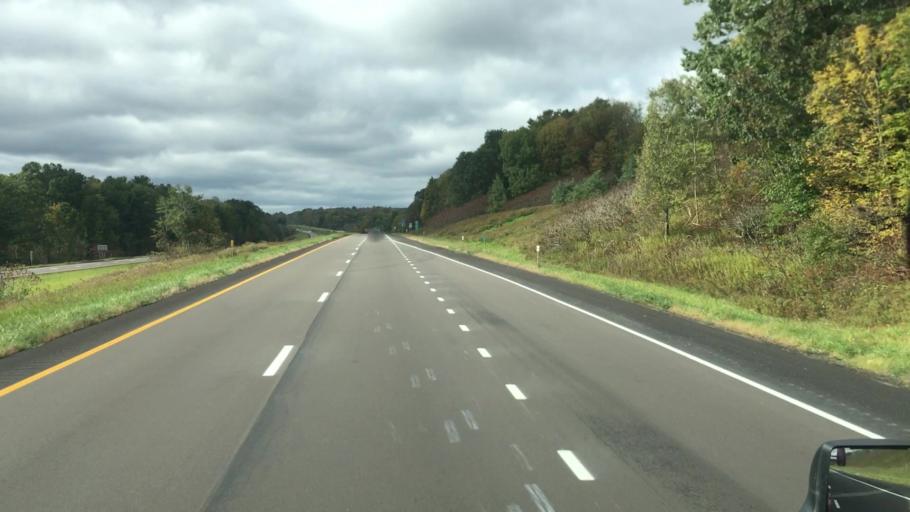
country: US
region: New York
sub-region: Chautauqua County
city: Celoron
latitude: 42.1266
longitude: -79.2805
